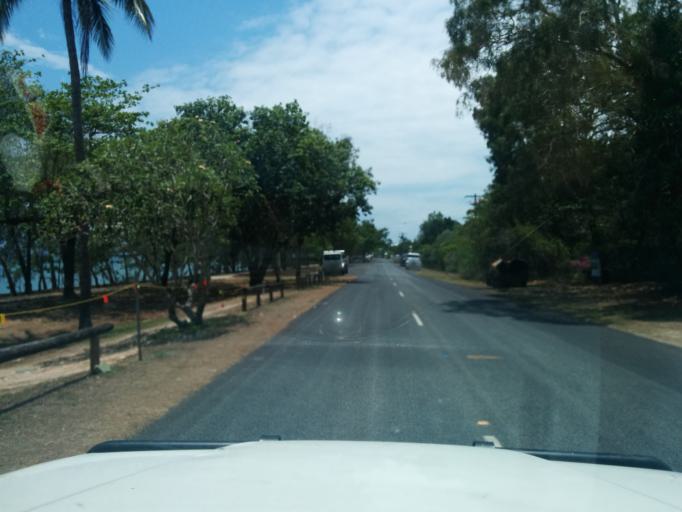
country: AU
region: Queensland
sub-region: Cairns
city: Yorkeys Knob
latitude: -16.8334
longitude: 145.7372
